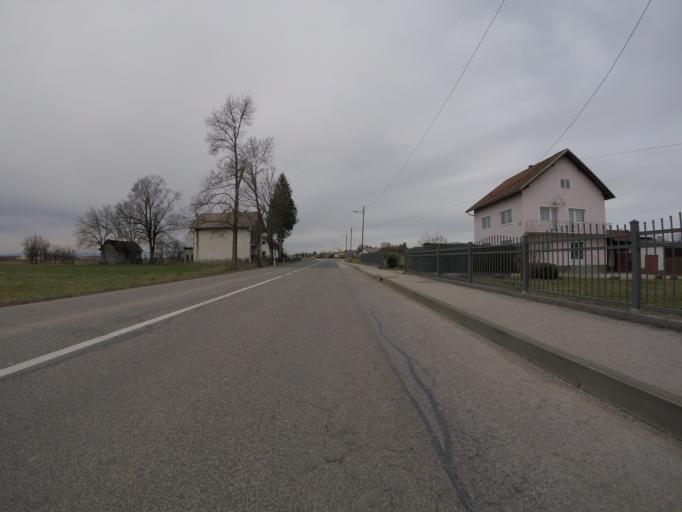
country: HR
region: Grad Zagreb
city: Horvati
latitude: 45.5795
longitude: 15.8597
